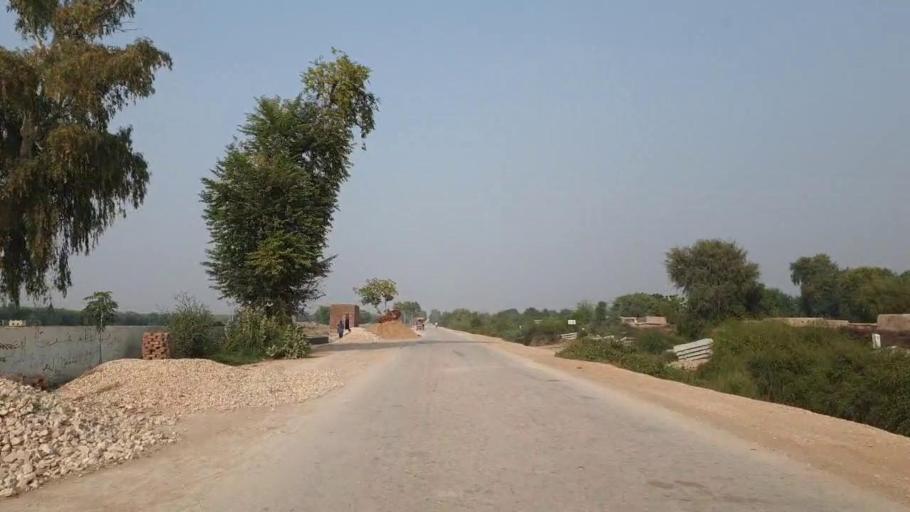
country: PK
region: Sindh
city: Bhan
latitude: 26.5809
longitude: 67.7285
